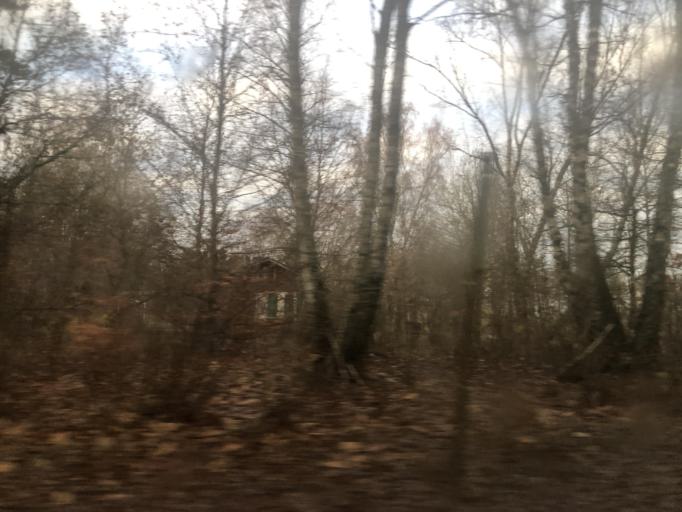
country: SE
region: Skane
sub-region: Sjobo Kommun
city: Blentarp
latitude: 55.6175
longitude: 13.5481
